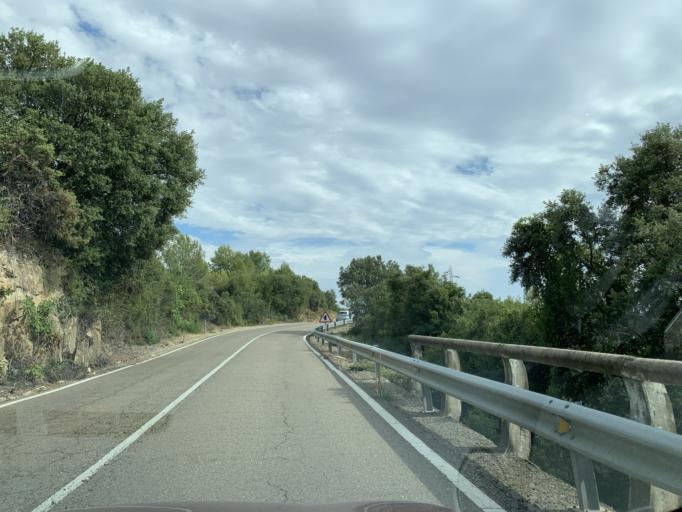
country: ES
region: Aragon
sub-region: Provincia de Zaragoza
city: Santa Eulalia de Gallego
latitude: 42.3159
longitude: -0.7537
